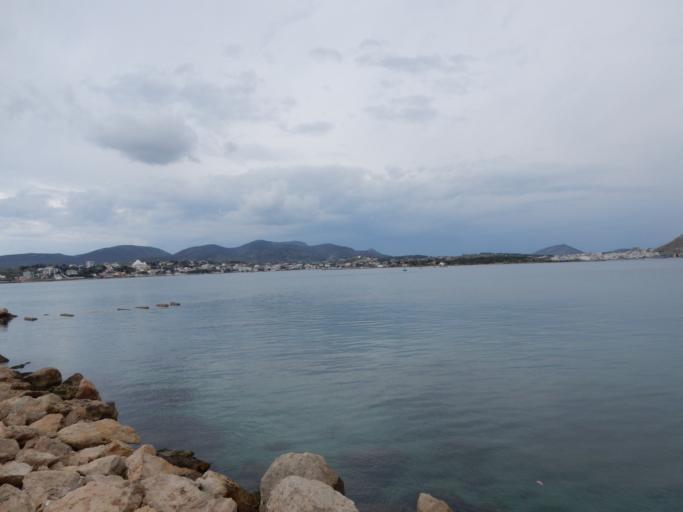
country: GR
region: Attica
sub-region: Nomos Piraios
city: Perama
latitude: 37.9650
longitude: 23.5524
